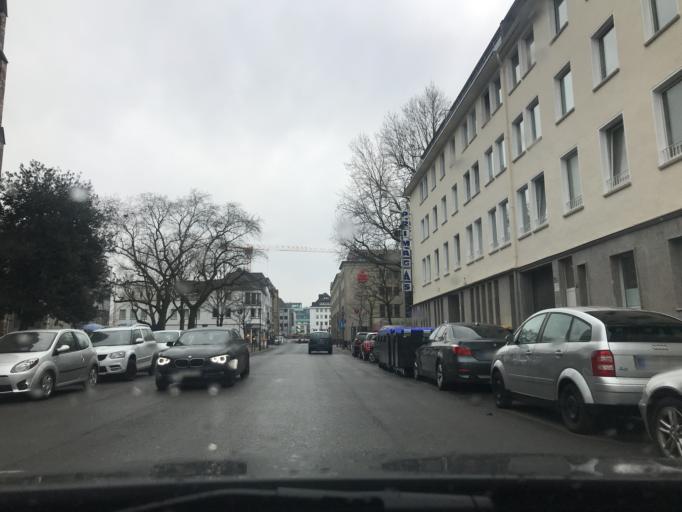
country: DE
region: North Rhine-Westphalia
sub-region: Regierungsbezirk Dusseldorf
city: Krefeld
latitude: 51.3329
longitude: 6.5694
